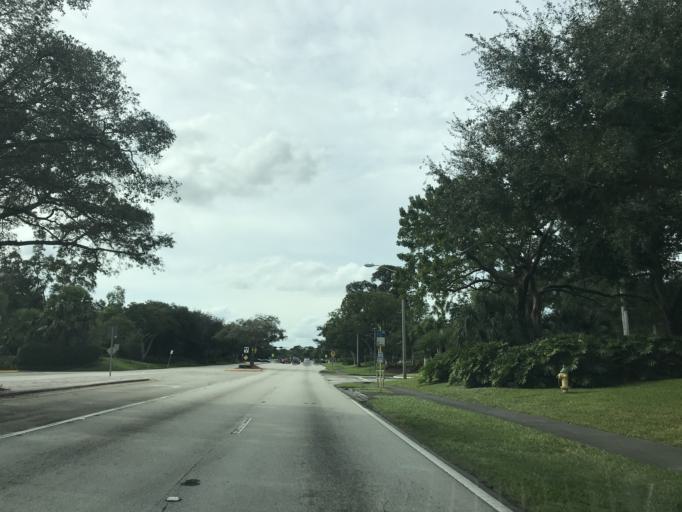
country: US
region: Florida
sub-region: Broward County
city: Coconut Creek
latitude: 26.2598
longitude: -80.1837
